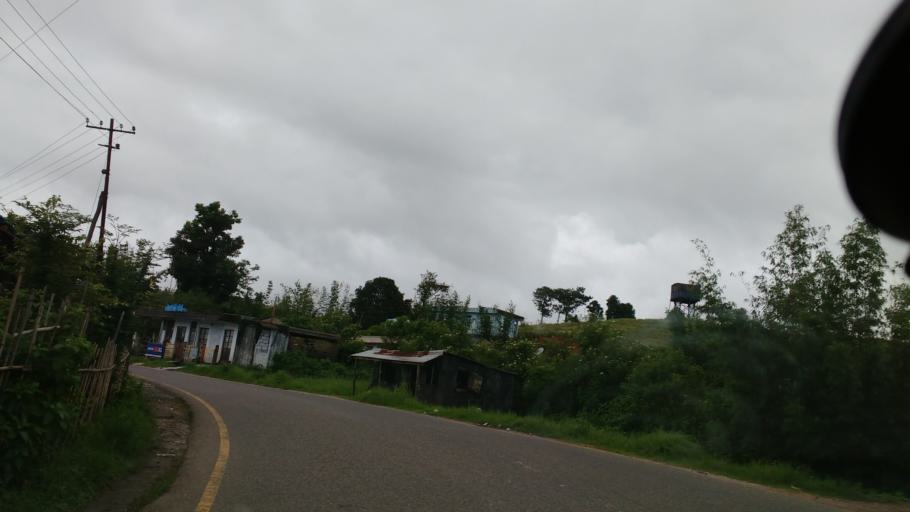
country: IN
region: Meghalaya
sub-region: East Khasi Hills
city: Cherrapunji
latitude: 25.2746
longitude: 91.7317
